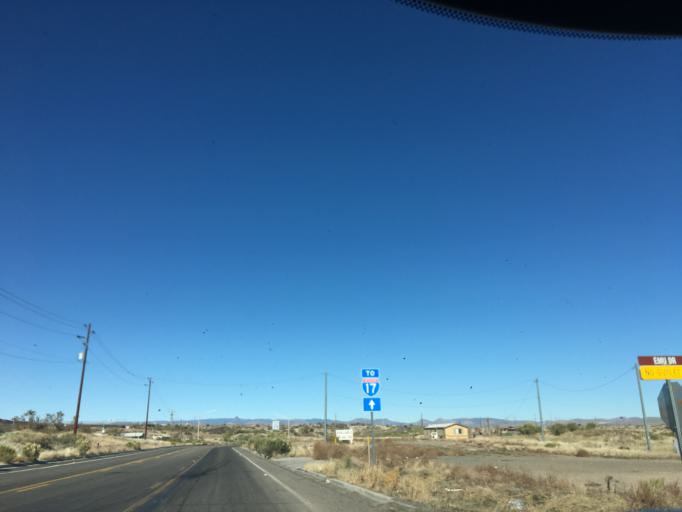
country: US
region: Arizona
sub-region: Yavapai County
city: Cordes Lakes
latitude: 34.3277
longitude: -112.1186
